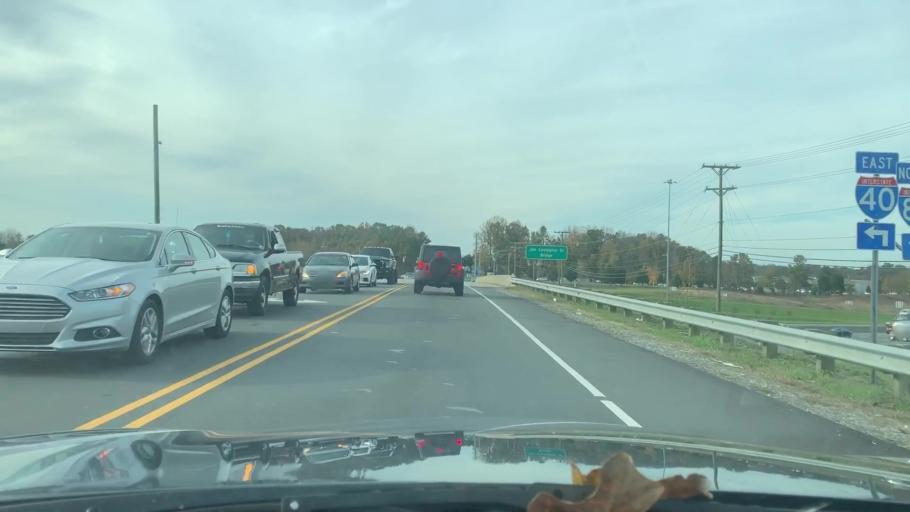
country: US
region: North Carolina
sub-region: Alamance County
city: Haw River
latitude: 36.0694
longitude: -79.3528
